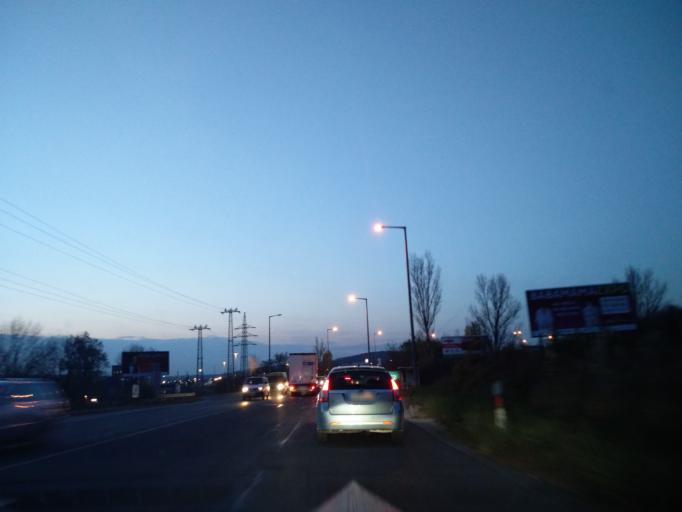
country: HU
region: Pest
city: Toeroekbalint
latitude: 47.4575
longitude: 18.9042
